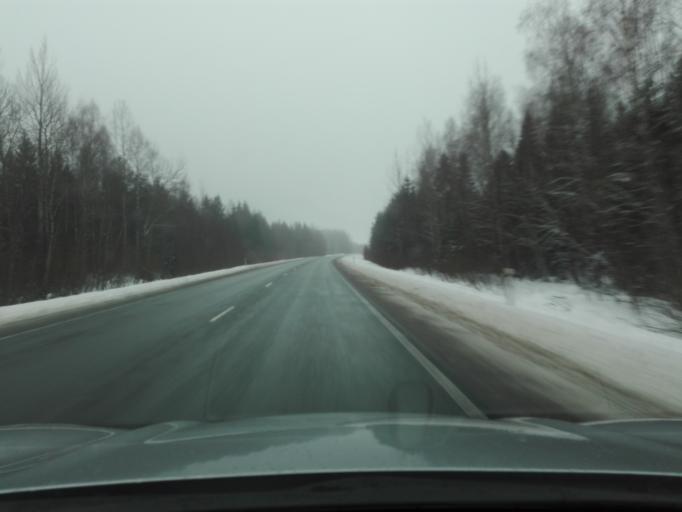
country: EE
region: Raplamaa
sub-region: Kohila vald
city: Kohila
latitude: 59.1338
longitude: 24.7920
